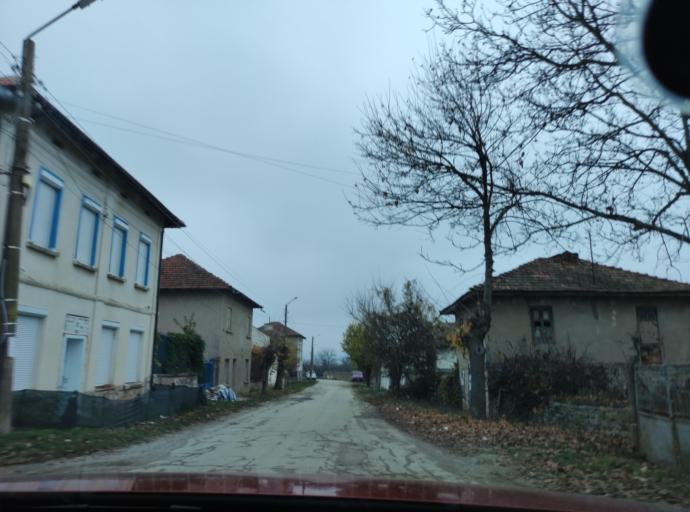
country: BG
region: Lovech
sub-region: Obshtina Yablanitsa
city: Yablanitsa
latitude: 43.0936
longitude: 24.0786
